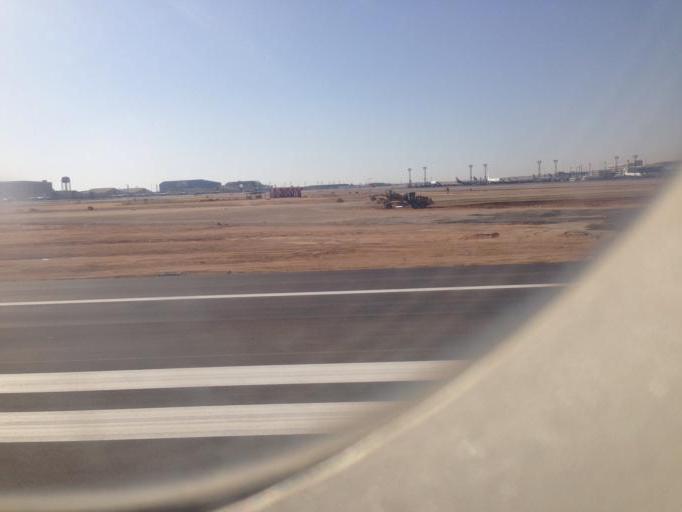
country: EG
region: Muhafazat al Qalyubiyah
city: Al Khankah
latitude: 30.1355
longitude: 31.4014
